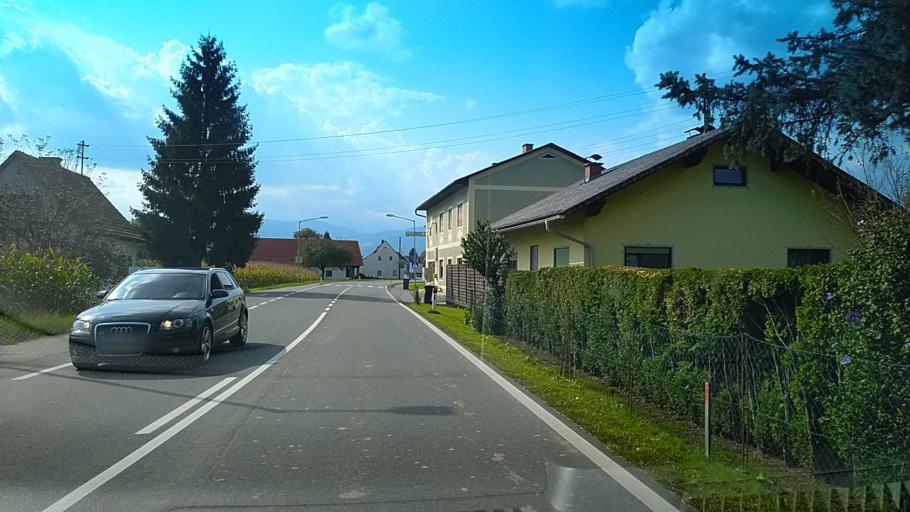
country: AT
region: Styria
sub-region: Politischer Bezirk Deutschlandsberg
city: Gross Sankt Florian
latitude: 46.8234
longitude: 15.2807
